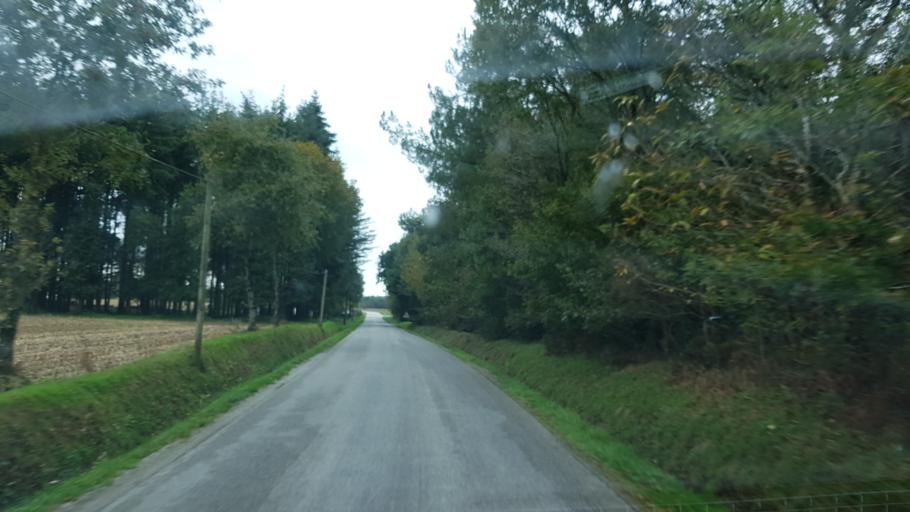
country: FR
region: Brittany
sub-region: Departement du Morbihan
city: Molac
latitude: 47.7803
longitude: -2.4643
